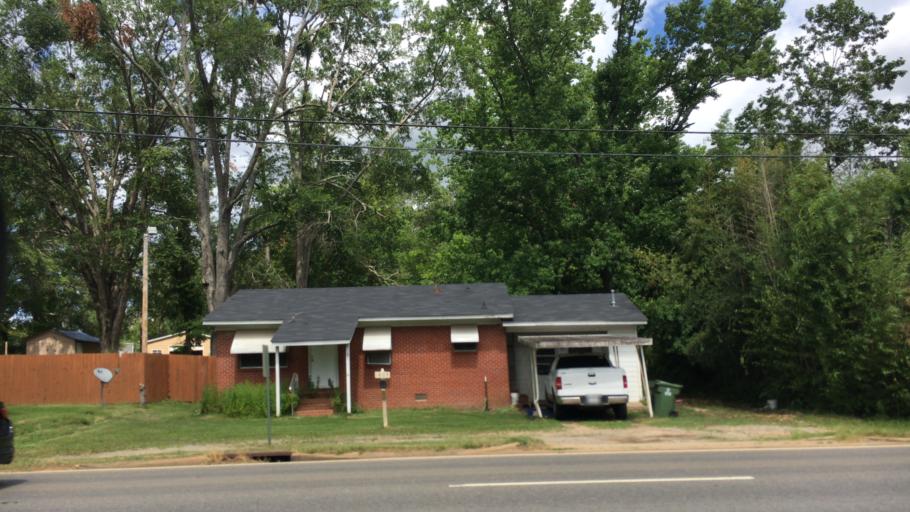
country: US
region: Louisiana
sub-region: Lincoln Parish
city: Ruston
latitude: 32.5086
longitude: -92.6375
